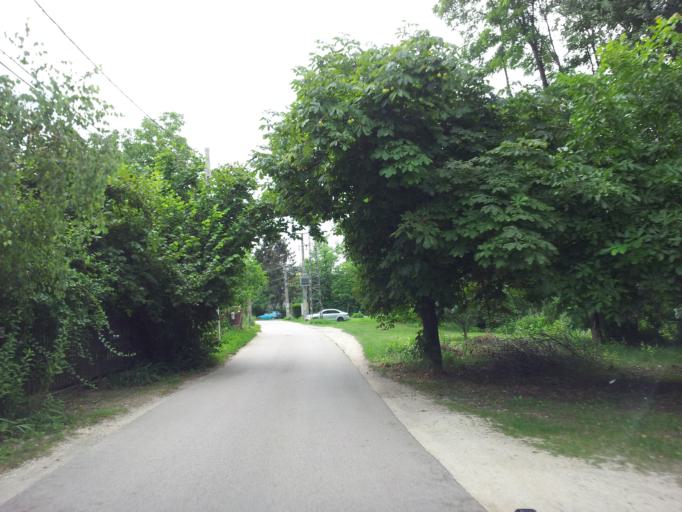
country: HU
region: Pest
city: Rackeve
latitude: 47.1729
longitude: 18.9513
